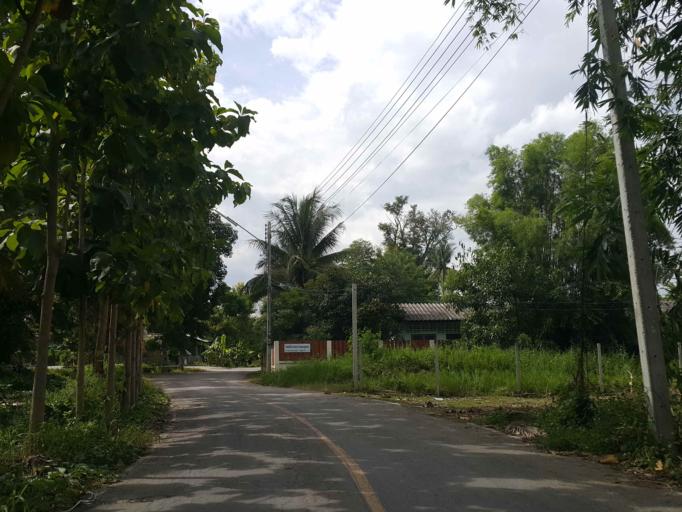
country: TH
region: Chiang Mai
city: Saraphi
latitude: 18.7361
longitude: 99.0576
